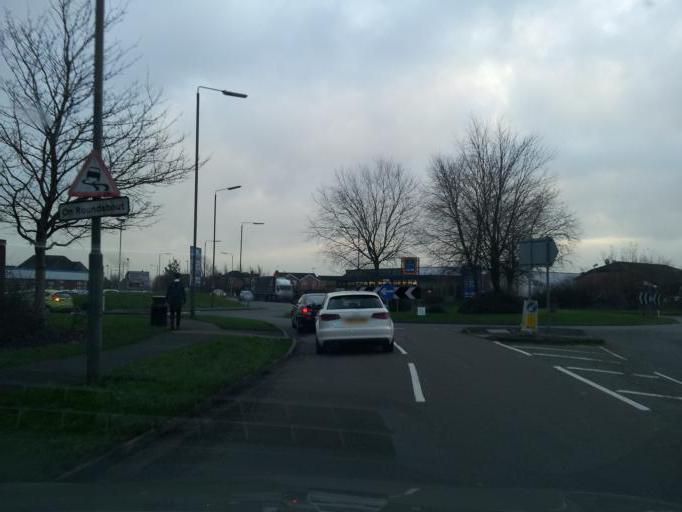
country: GB
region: England
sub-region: Derbyshire
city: Etwall
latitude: 52.8722
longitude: -1.6281
